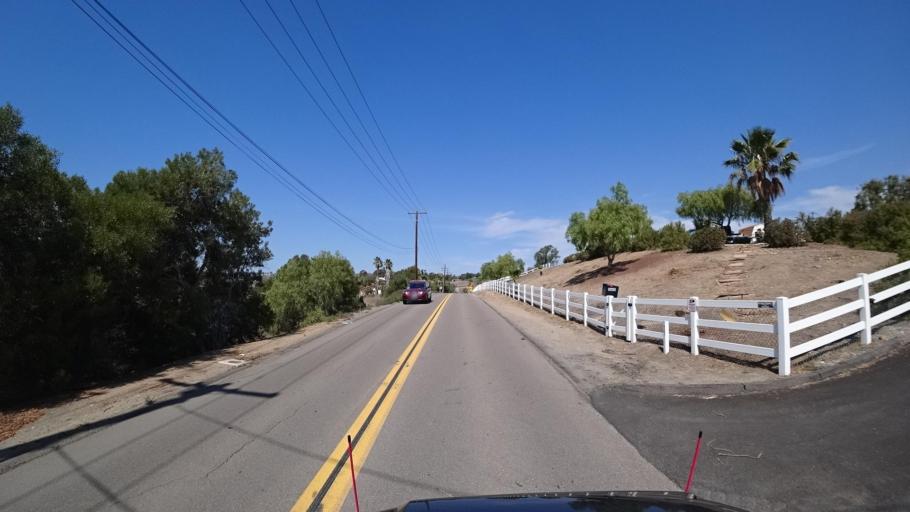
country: US
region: California
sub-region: San Diego County
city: La Presa
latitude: 32.6742
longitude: -116.9980
